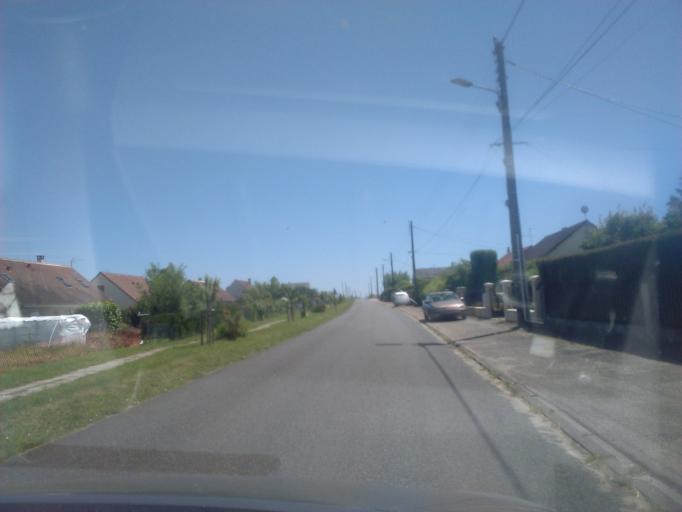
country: FR
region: Centre
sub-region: Departement du Loir-et-Cher
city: Herbault
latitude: 47.6501
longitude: 1.1849
